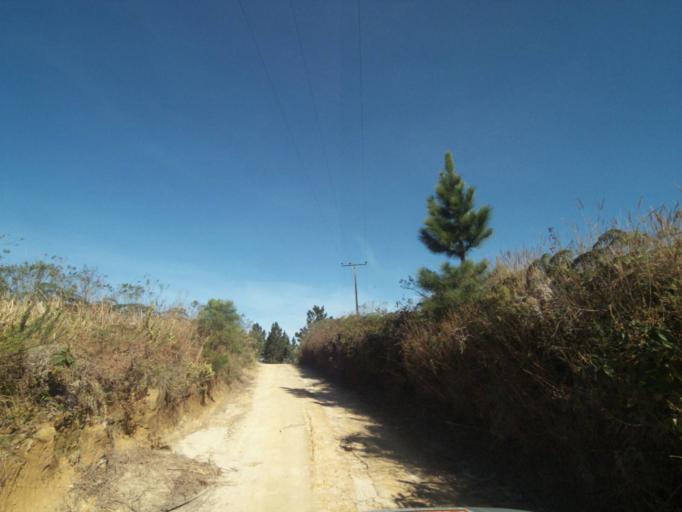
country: BR
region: Parana
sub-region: Tibagi
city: Tibagi
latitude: -24.5663
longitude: -50.4709
